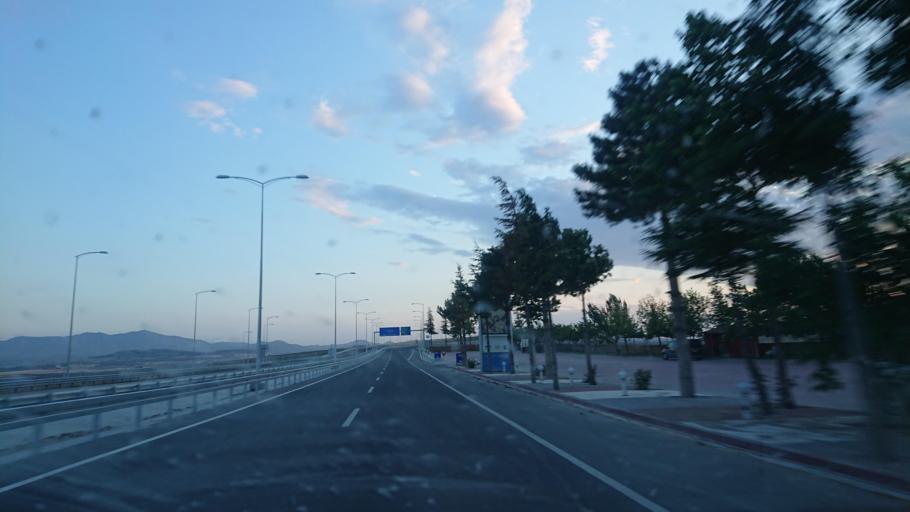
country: TR
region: Aksaray
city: Balci
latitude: 38.7752
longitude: 34.1093
